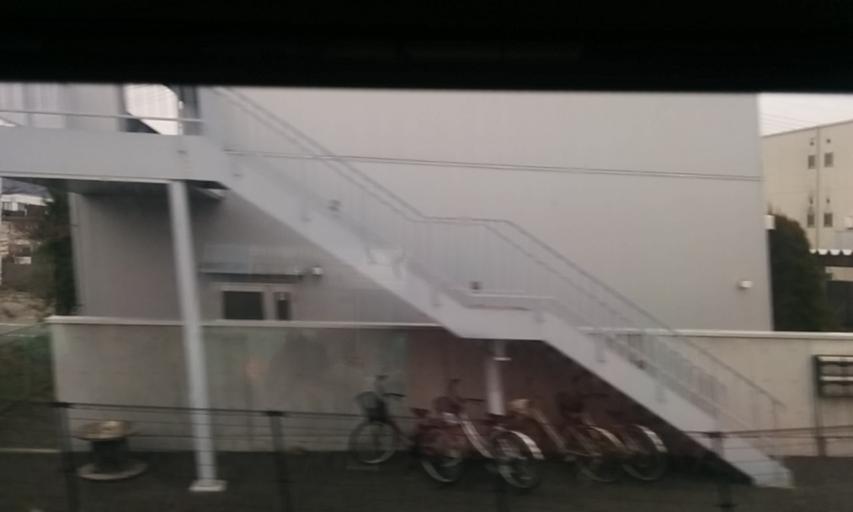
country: JP
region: Nagano
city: Matsumoto
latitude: 36.1963
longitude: 137.9643
